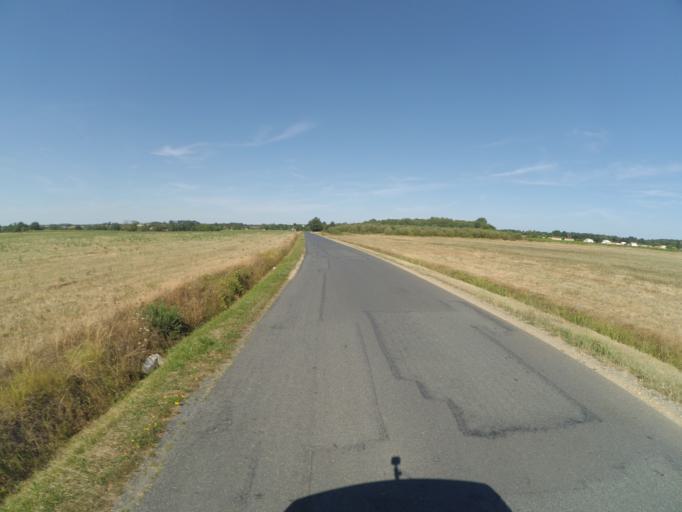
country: FR
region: Pays de la Loire
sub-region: Departement de la Loire-Atlantique
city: Vallet
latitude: 47.1743
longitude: -1.2739
